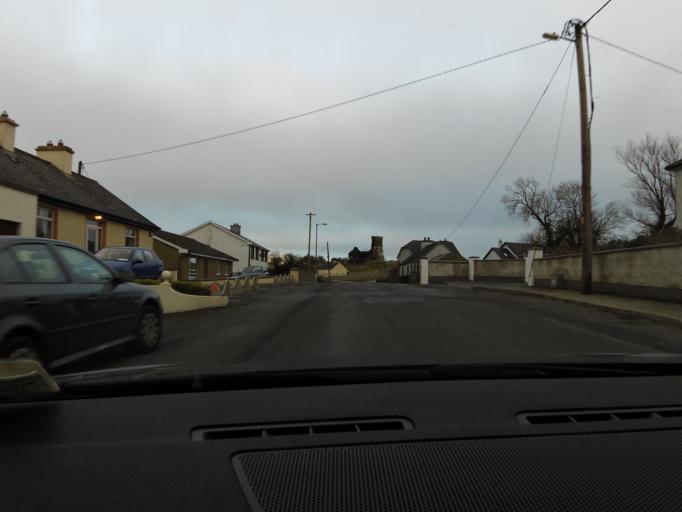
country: IE
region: Connaught
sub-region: Sligo
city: Ballymote
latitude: 53.9921
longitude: -8.5132
